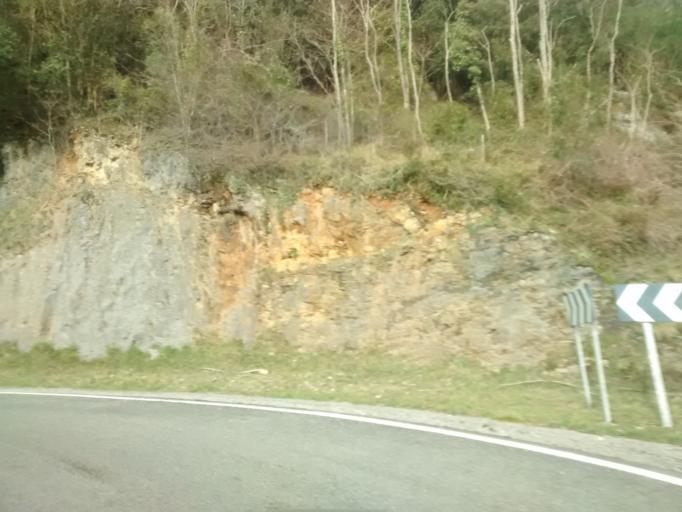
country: ES
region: Cantabria
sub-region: Provincia de Cantabria
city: Arredondo
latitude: 43.2799
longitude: -3.6114
